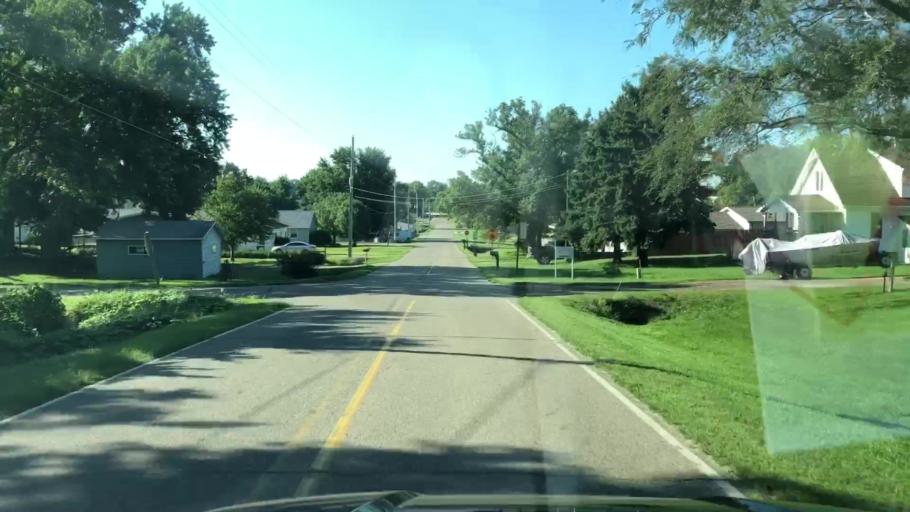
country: US
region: Iowa
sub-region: Woodbury County
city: Sergeant Bluff
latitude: 42.4118
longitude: -96.2138
